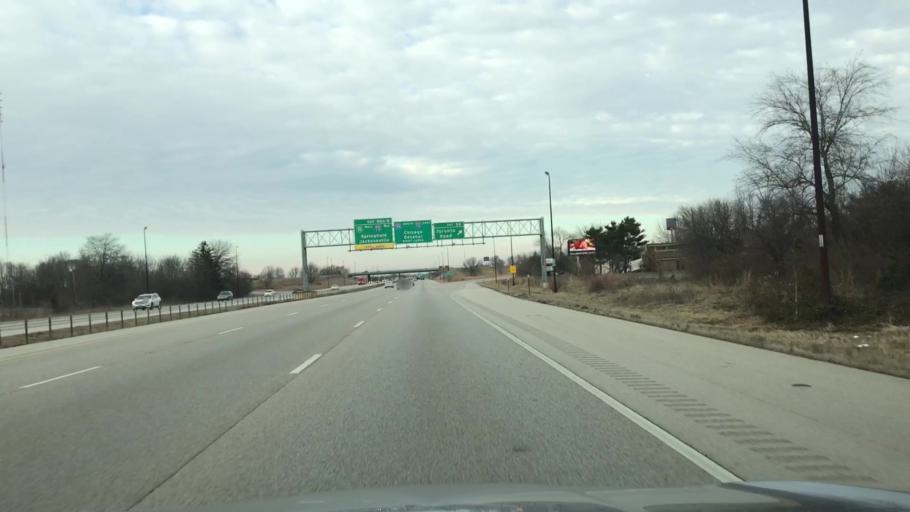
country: US
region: Illinois
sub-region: Sangamon County
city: Southern View
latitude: 39.7084
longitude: -89.6436
